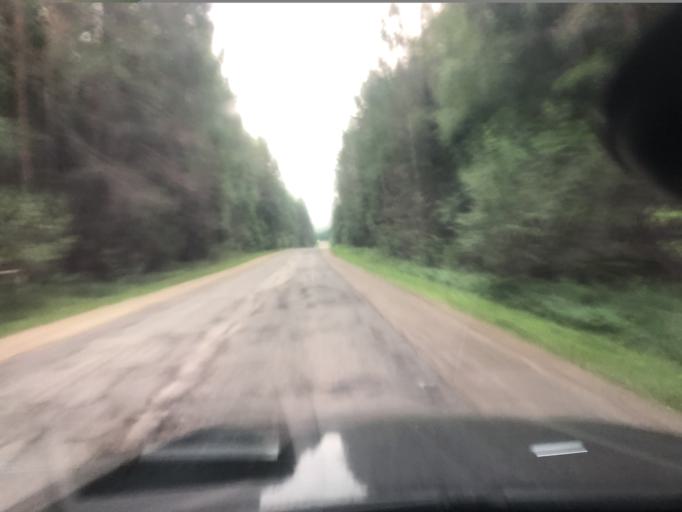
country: RU
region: Jaroslavl
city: Petrovsk
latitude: 57.0001
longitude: 39.0802
